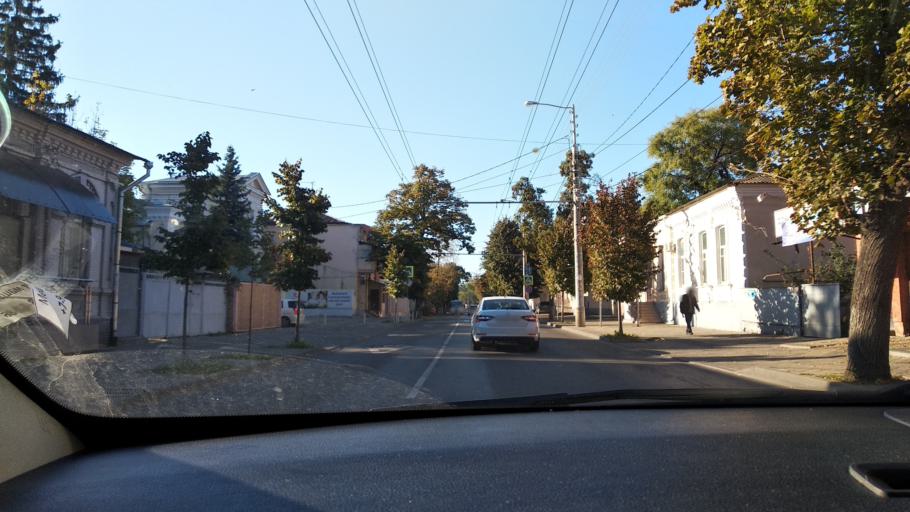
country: RU
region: Krasnodarskiy
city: Krasnodar
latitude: 45.0187
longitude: 38.9753
